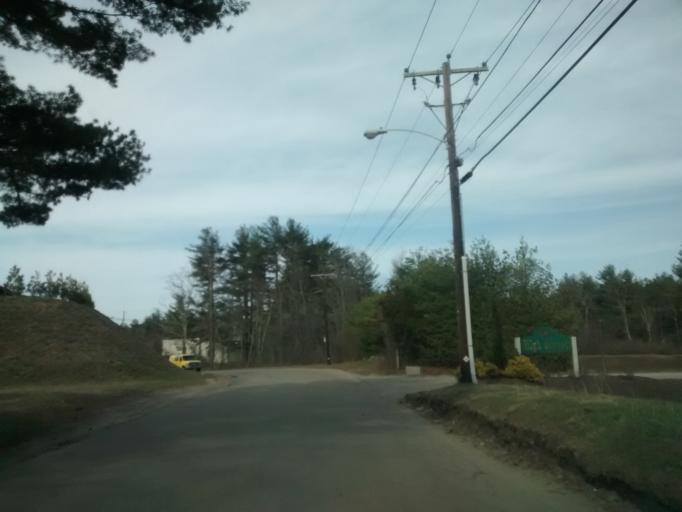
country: US
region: Massachusetts
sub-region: Norfolk County
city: Plainville
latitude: 42.0264
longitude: -71.3518
